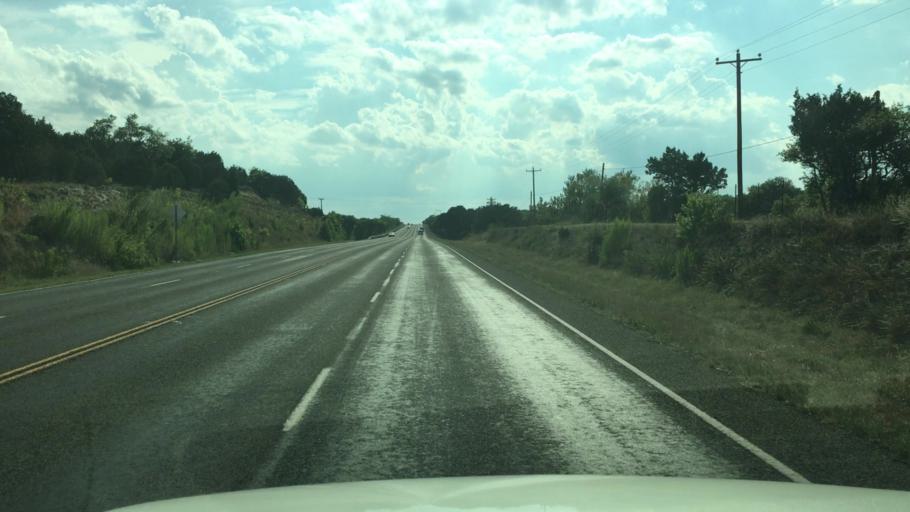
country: US
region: Texas
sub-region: Blanco County
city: Johnson City
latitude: 30.2102
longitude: -98.2888
